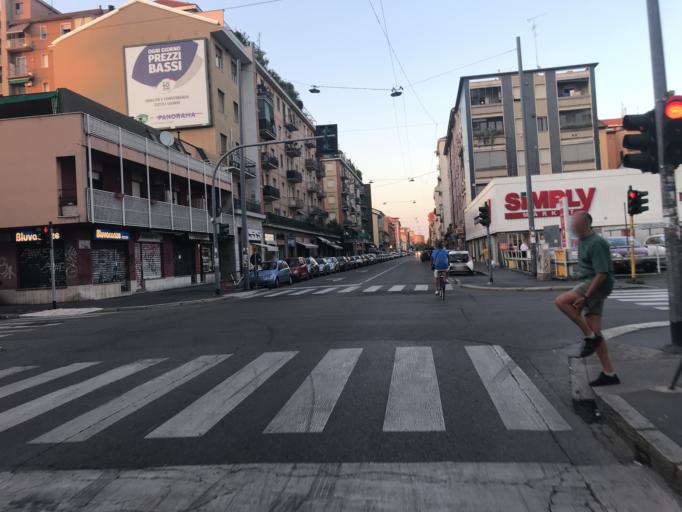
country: IT
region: Lombardy
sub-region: Citta metropolitana di Milano
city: Sesto San Giovanni
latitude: 45.5036
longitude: 9.2398
